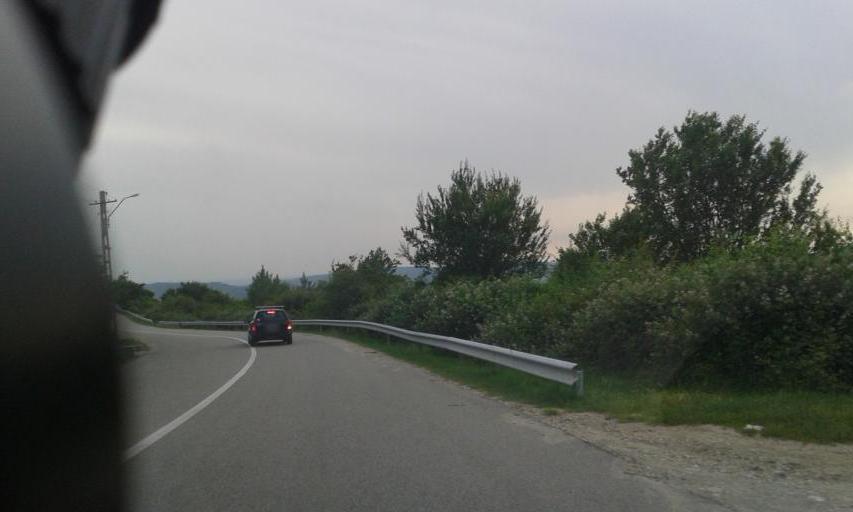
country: RO
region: Gorj
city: Novaci-Straini
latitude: 45.1899
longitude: 23.6833
